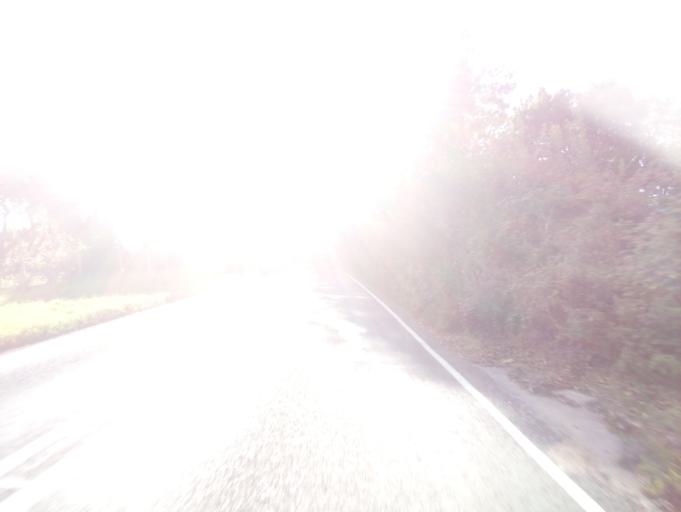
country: GB
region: England
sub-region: Devon
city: Newton Poppleford
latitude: 50.6981
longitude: -3.3192
